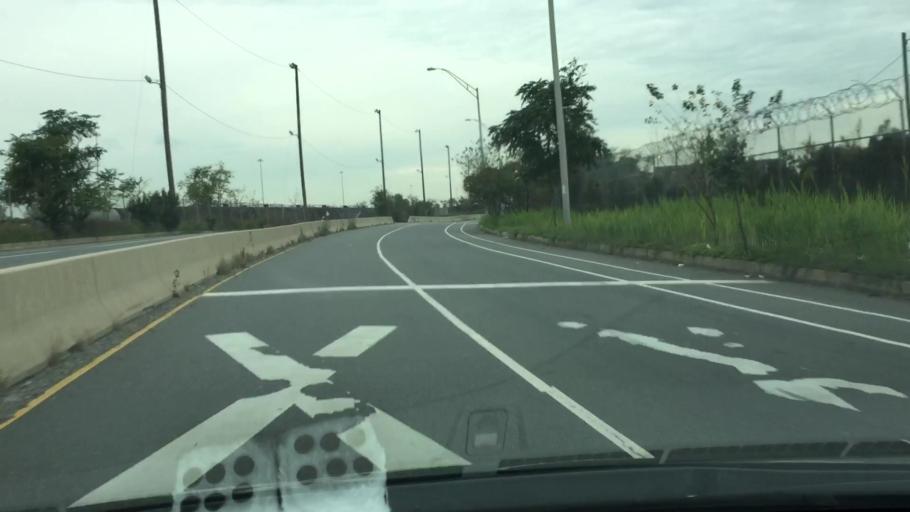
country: US
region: New Jersey
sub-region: Camden County
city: Gloucester City
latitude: 39.9022
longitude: -75.1427
